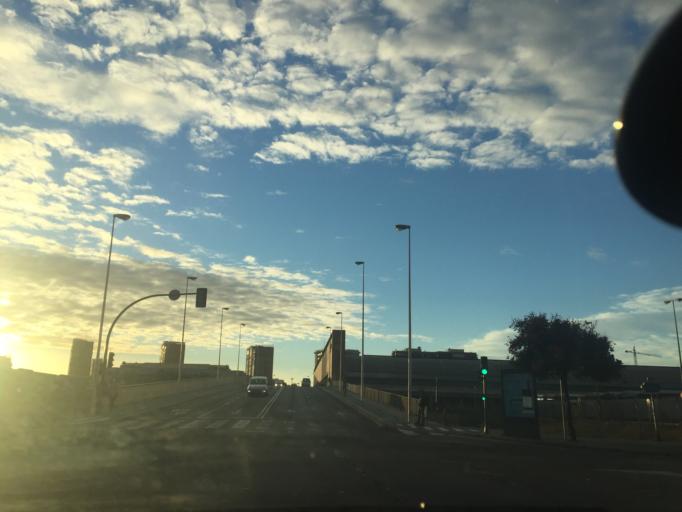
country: ES
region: Andalusia
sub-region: Provincia de Sevilla
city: Sevilla
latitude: 37.3956
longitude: -5.9740
